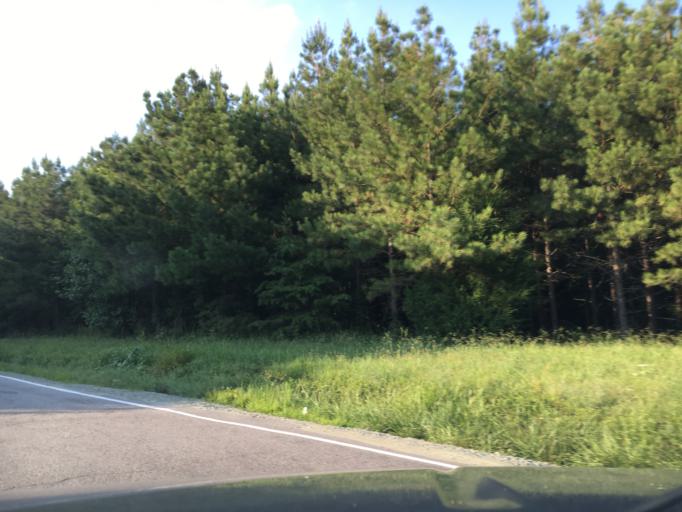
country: US
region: Virginia
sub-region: Pittsylvania County
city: Chatham
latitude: 36.8130
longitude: -79.2636
